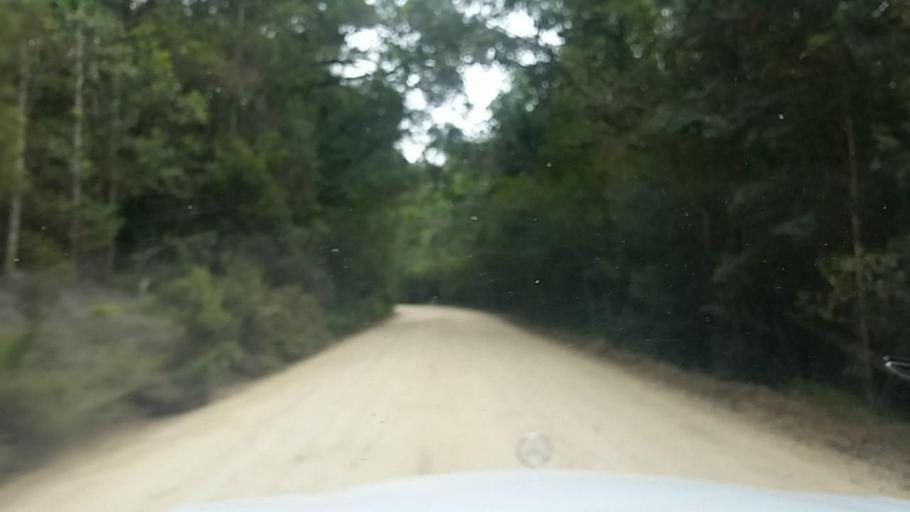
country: ZA
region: Western Cape
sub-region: Eden District Municipality
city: Knysna
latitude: -33.9487
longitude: 23.1514
